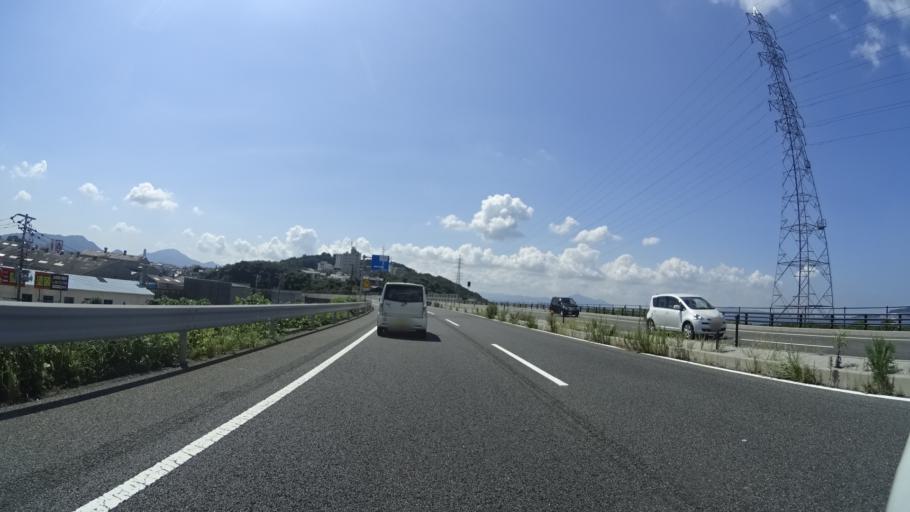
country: JP
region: Yamaguchi
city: Shimonoseki
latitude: 33.9777
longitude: 130.9175
